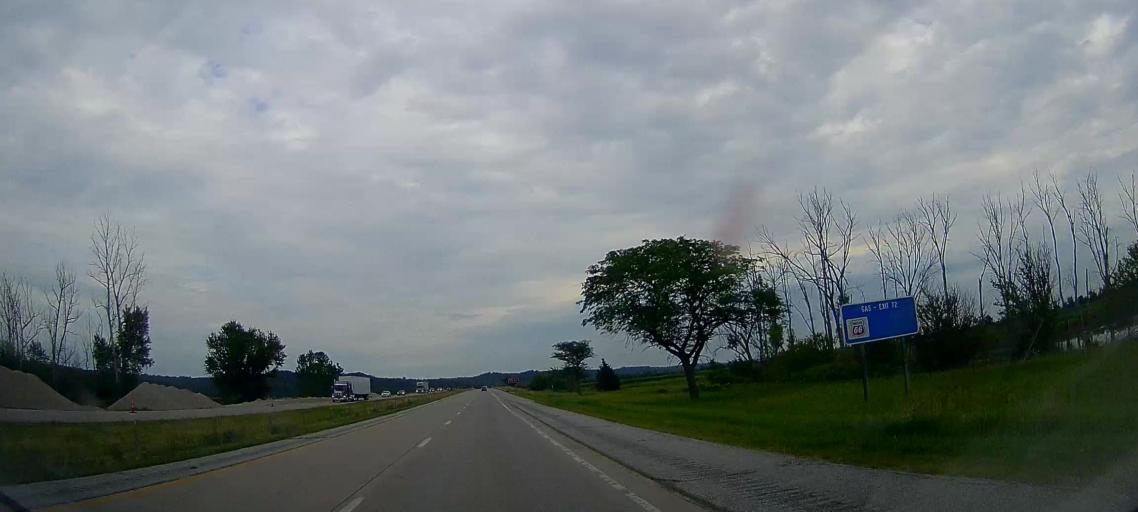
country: US
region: Iowa
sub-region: Harrison County
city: Missouri Valley
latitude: 41.5114
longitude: -95.9108
